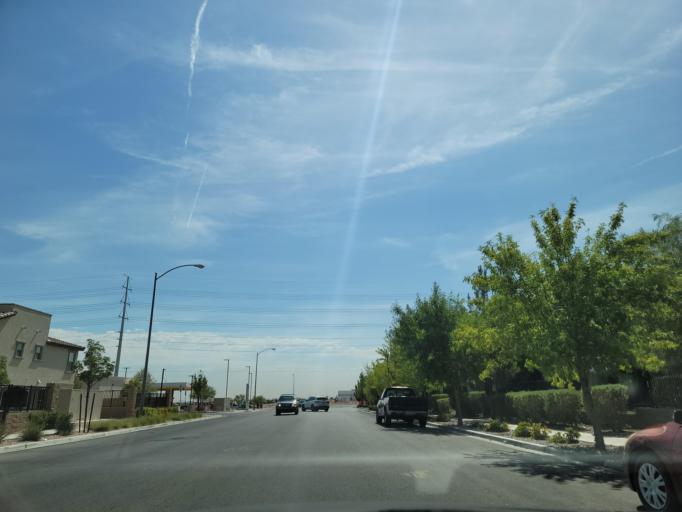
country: US
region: Nevada
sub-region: Clark County
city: Spring Valley
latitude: 36.0740
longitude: -115.2812
